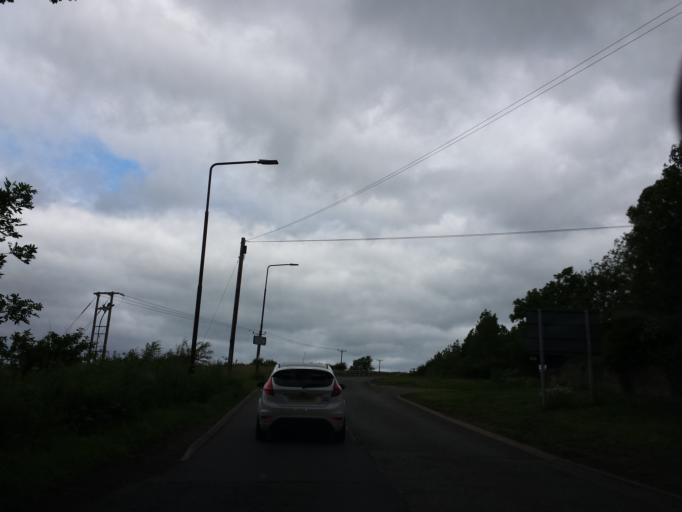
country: GB
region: Scotland
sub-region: East Lothian
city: Haddington
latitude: 55.9610
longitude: -2.7904
